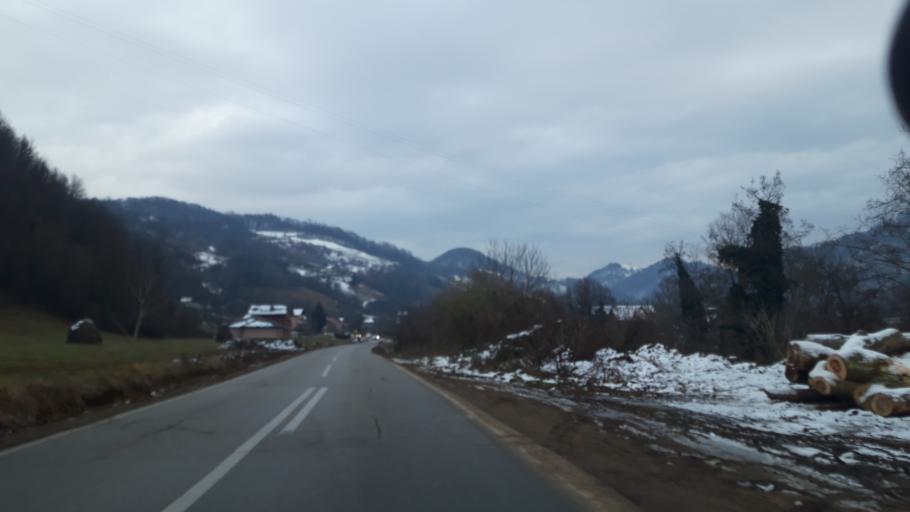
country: BA
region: Republika Srpska
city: Milici
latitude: 44.2194
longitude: 19.1029
